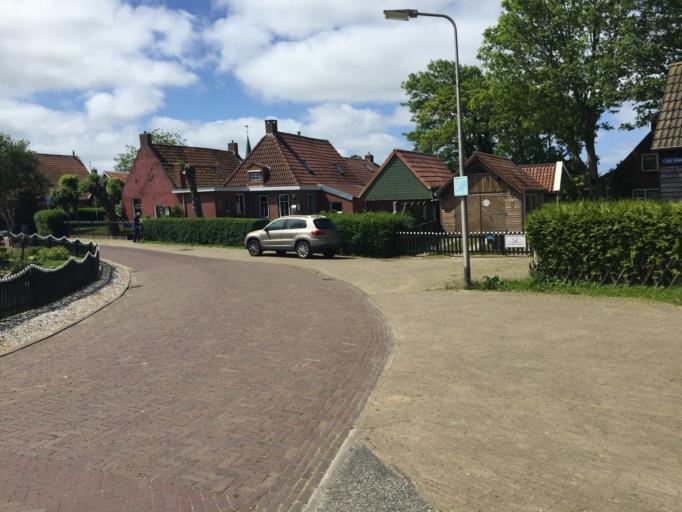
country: NL
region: Friesland
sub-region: Gemeente Dongeradeel
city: Anjum
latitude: 53.4028
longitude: 6.0838
